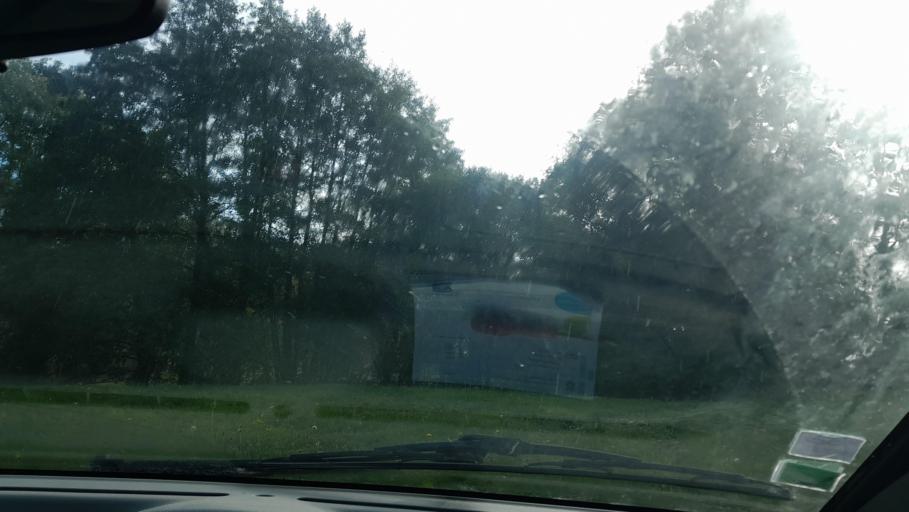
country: FR
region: Pays de la Loire
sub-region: Departement de la Mayenne
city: Cosse-le-Vivien
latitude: 47.9358
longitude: -0.8970
